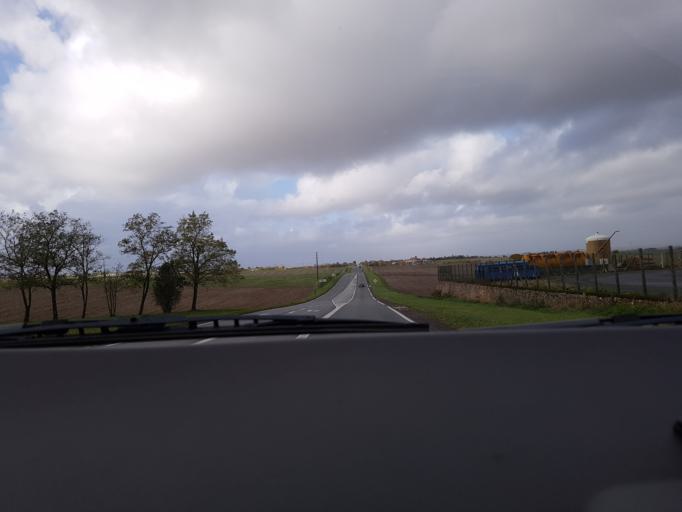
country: FR
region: Poitou-Charentes
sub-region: Departement de la Charente-Maritime
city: Pons
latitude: 45.6407
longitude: -0.5799
